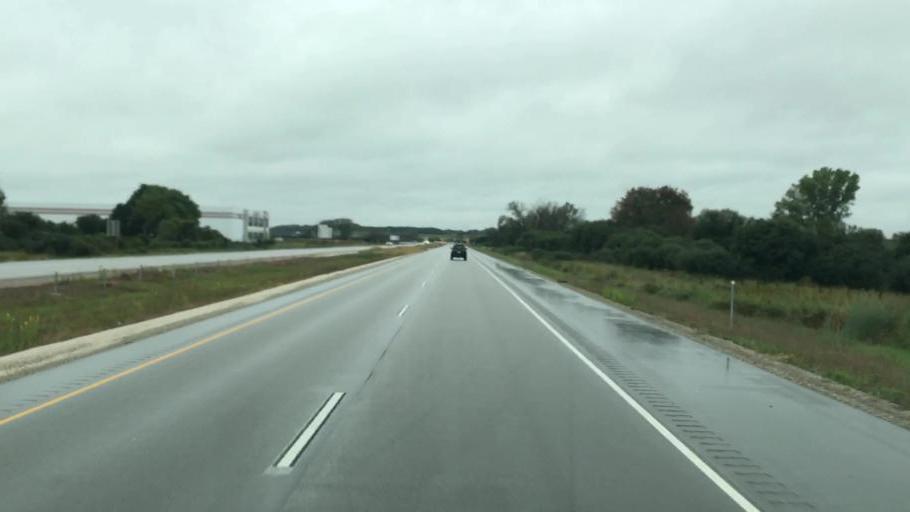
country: US
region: Wisconsin
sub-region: Waukesha County
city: Pewaukee
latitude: 43.0576
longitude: -88.2513
